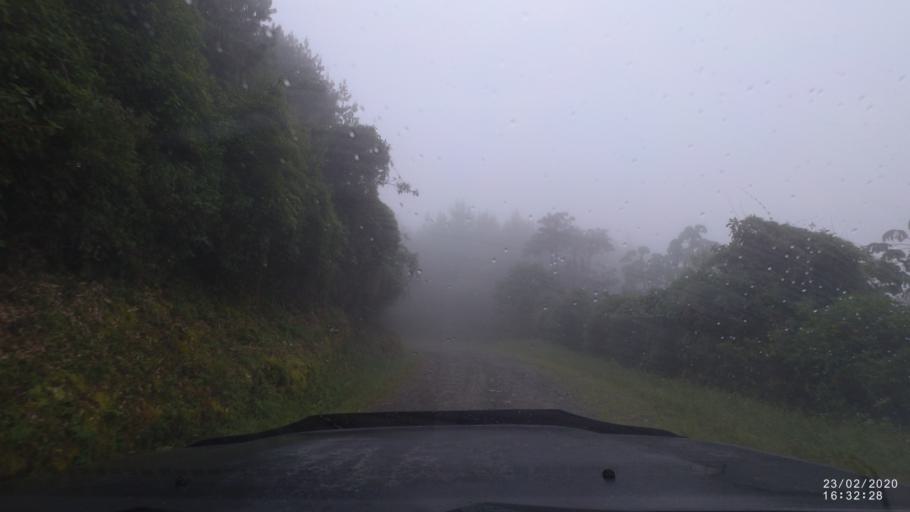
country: BO
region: Cochabamba
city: Colomi
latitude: -17.0931
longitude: -65.9916
